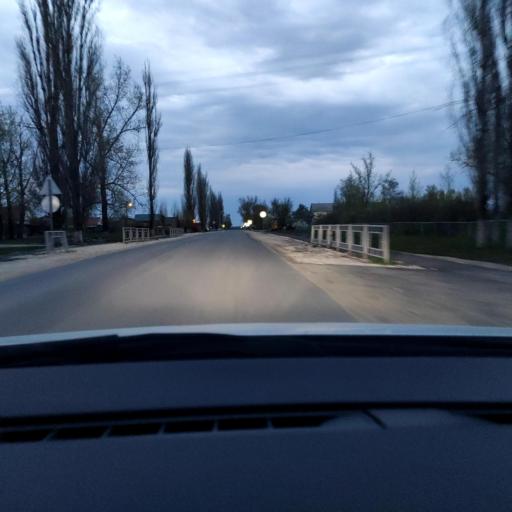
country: RU
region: Lipetsk
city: Donskoye
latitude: 52.6750
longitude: 38.9214
